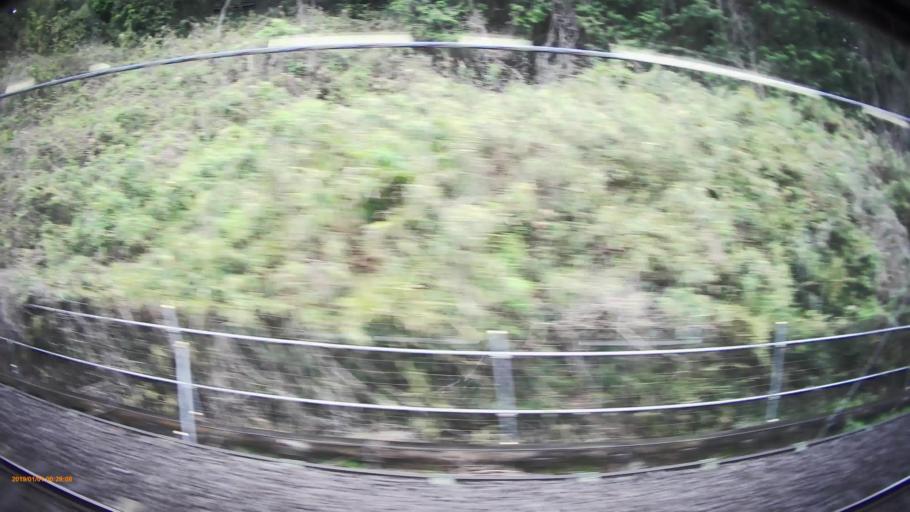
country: JP
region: Yamanashi
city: Uenohara
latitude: 35.6127
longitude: 139.0810
